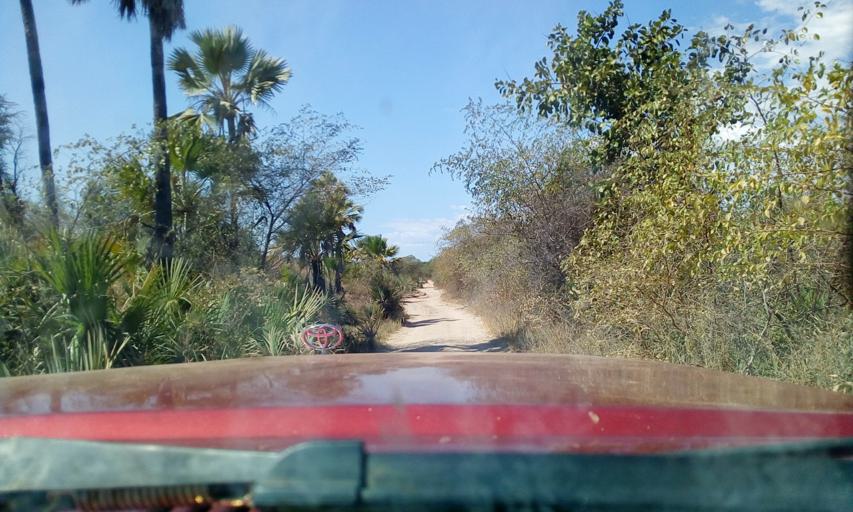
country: MG
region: Boeny
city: Sitampiky
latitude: -16.1270
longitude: 45.4861
